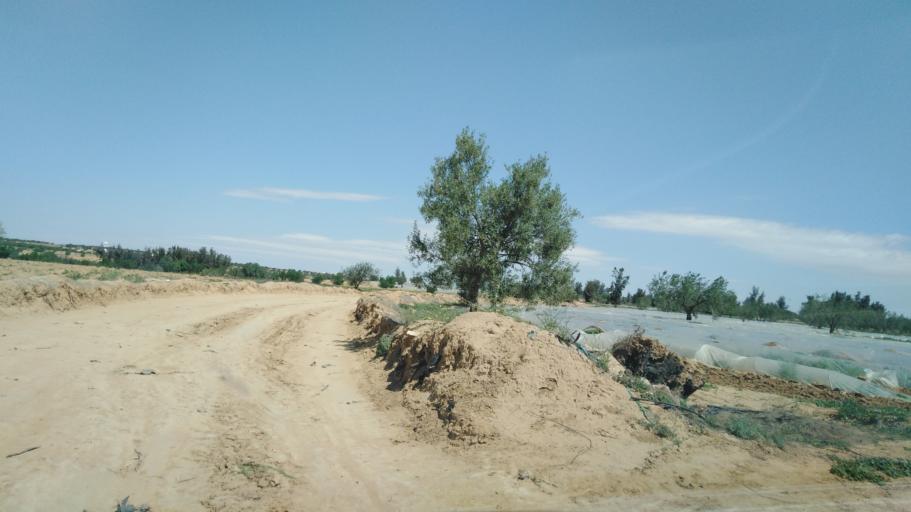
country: TN
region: Safaqis
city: Sfax
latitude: 34.7677
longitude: 10.5275
